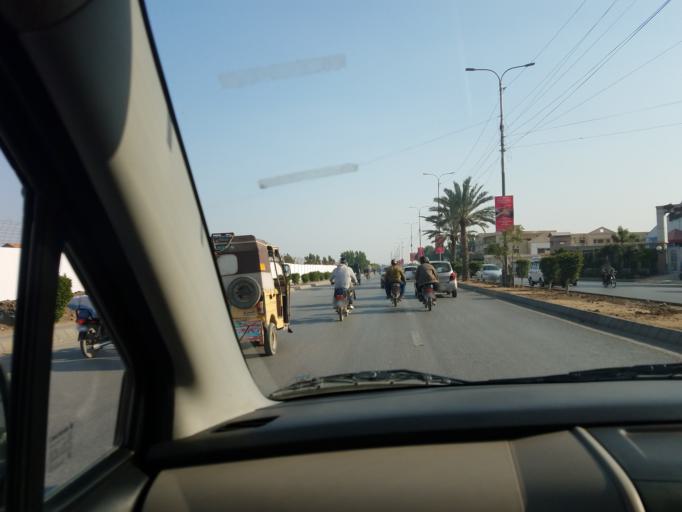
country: PK
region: Sindh
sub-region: Karachi District
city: Karachi
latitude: 24.8957
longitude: 67.1191
